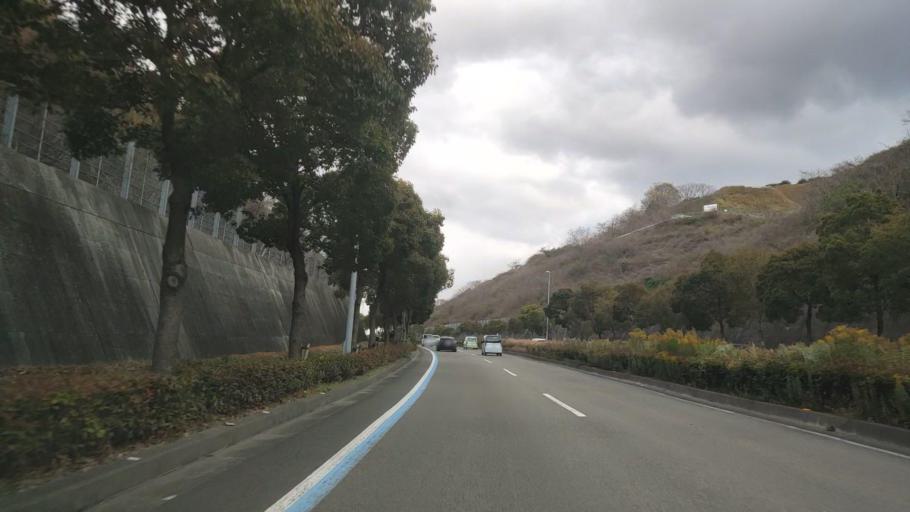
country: JP
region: Ehime
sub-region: Shikoku-chuo Shi
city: Matsuyama
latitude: 33.8883
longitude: 132.7556
